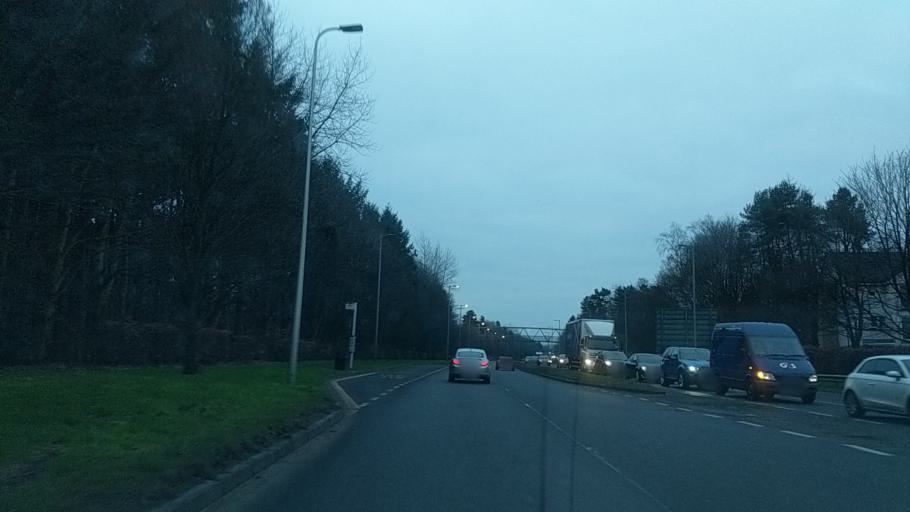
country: GB
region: Scotland
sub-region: South Lanarkshire
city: East Kilbride
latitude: 55.7747
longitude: -4.1632
